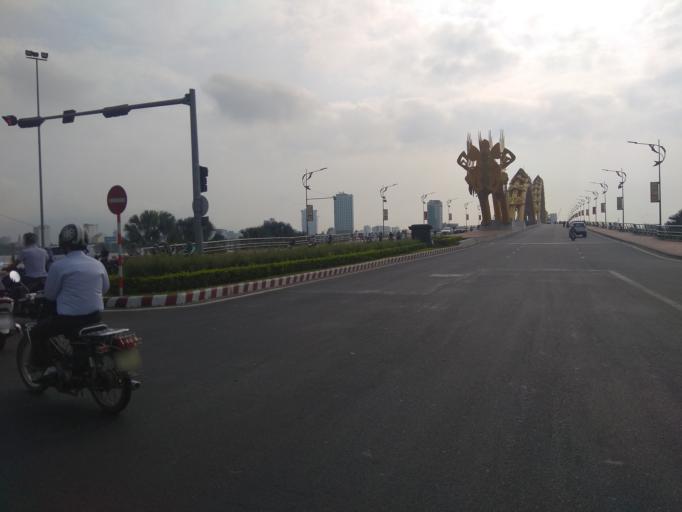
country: VN
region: Da Nang
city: Da Nang
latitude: 16.0610
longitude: 108.2240
